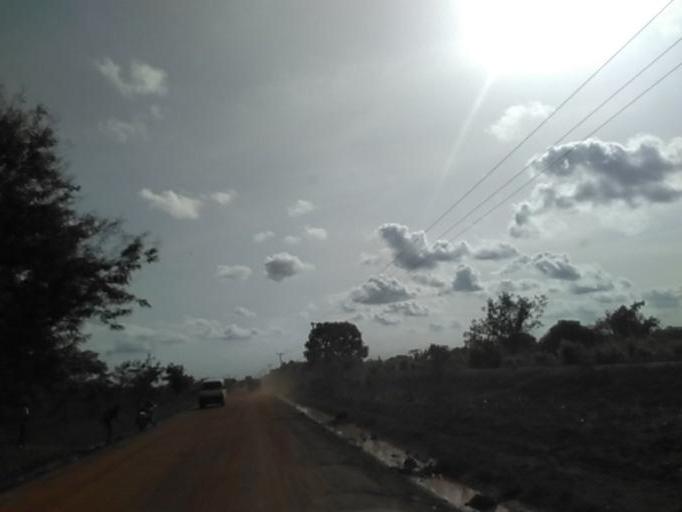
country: GH
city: Akropong
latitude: 6.0969
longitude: 0.2469
